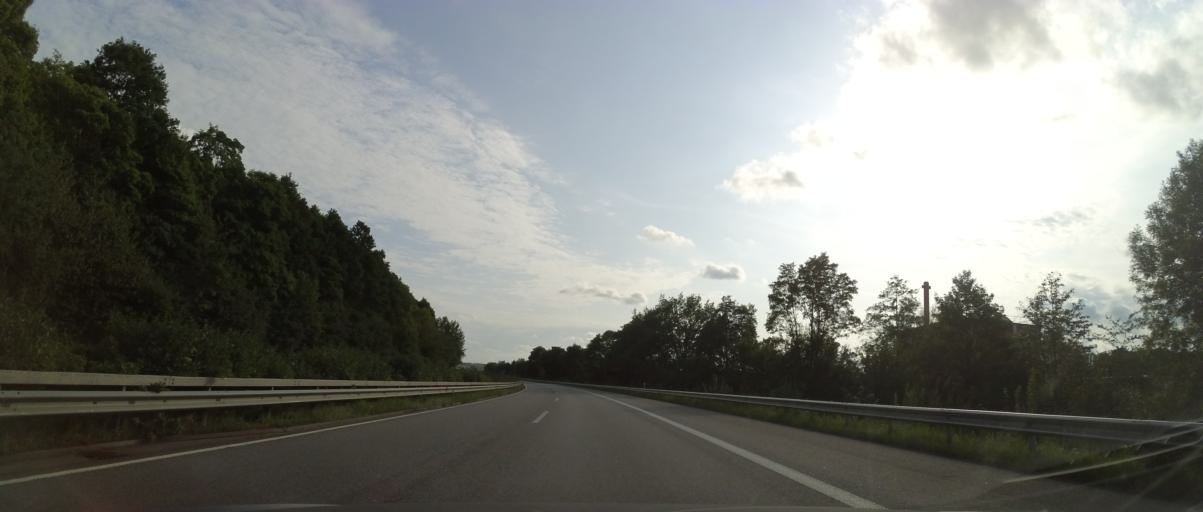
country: DE
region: Rheinland-Pfalz
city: Mehren
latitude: 50.1643
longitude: 6.8841
